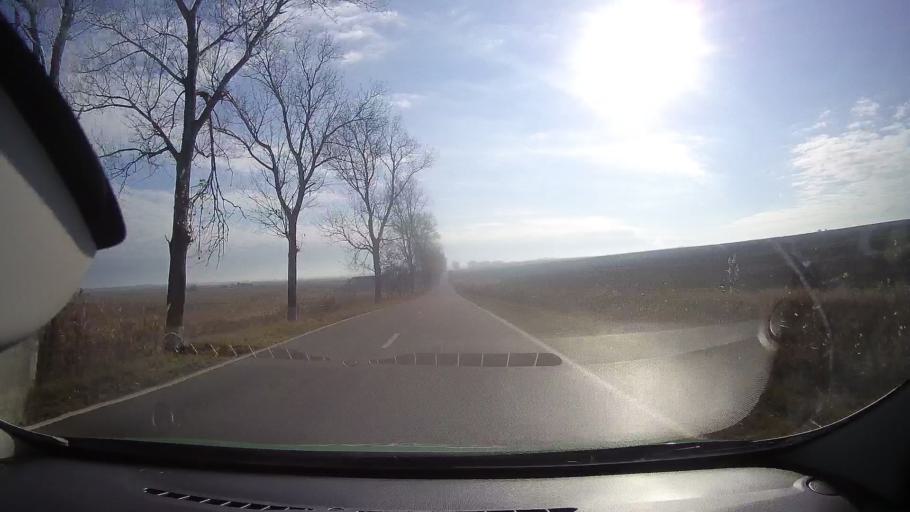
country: RO
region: Tulcea
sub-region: Comuna Mahmudia
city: Mahmudia
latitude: 45.0650
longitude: 29.1085
